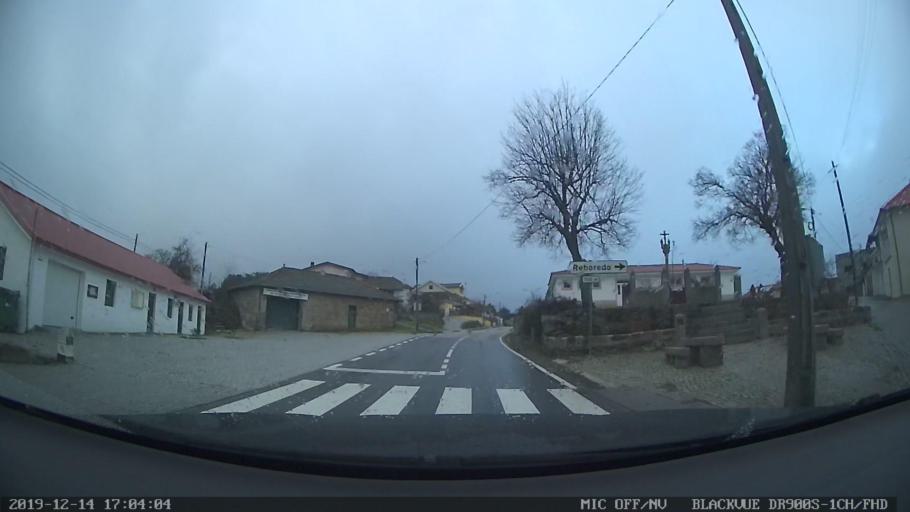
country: PT
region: Vila Real
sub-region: Vila Pouca de Aguiar
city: Vila Pouca de Aguiar
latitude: 41.4456
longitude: -7.5716
